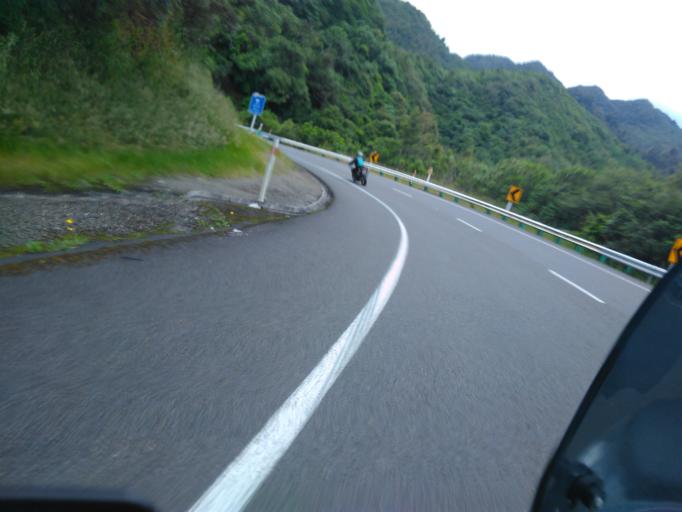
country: NZ
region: Bay of Plenty
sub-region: Opotiki District
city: Opotiki
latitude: -38.3388
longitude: 177.4221
